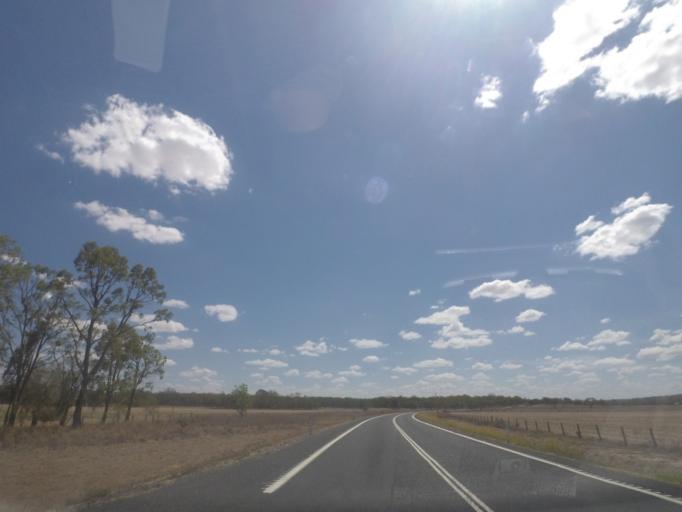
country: AU
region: Queensland
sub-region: Southern Downs
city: Warwick
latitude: -28.1834
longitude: 151.8164
